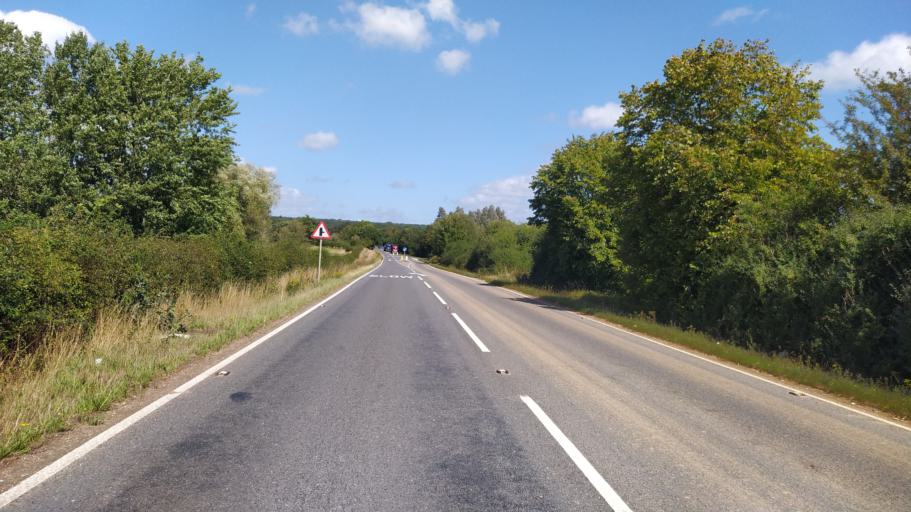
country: GB
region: England
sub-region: Hampshire
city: Lindford
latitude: 51.1451
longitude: -0.8498
